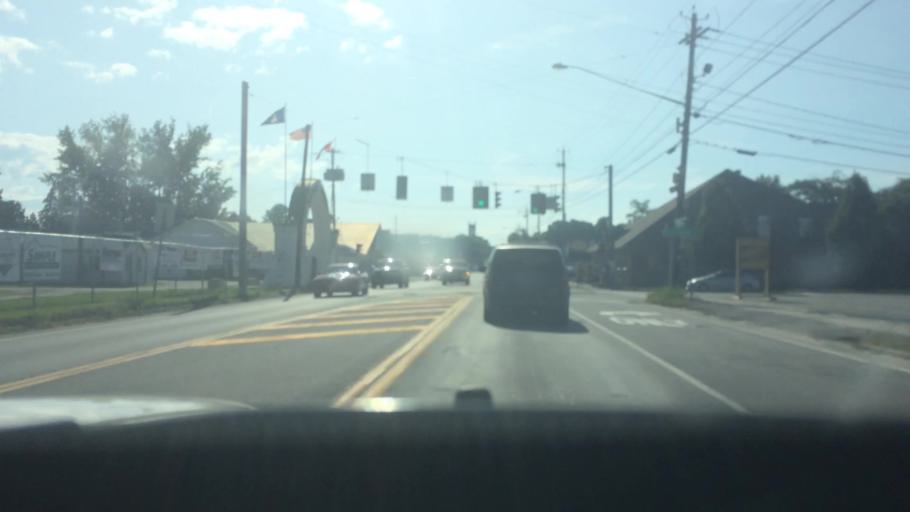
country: US
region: New York
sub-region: Franklin County
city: Malone
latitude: 44.8503
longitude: -74.2779
